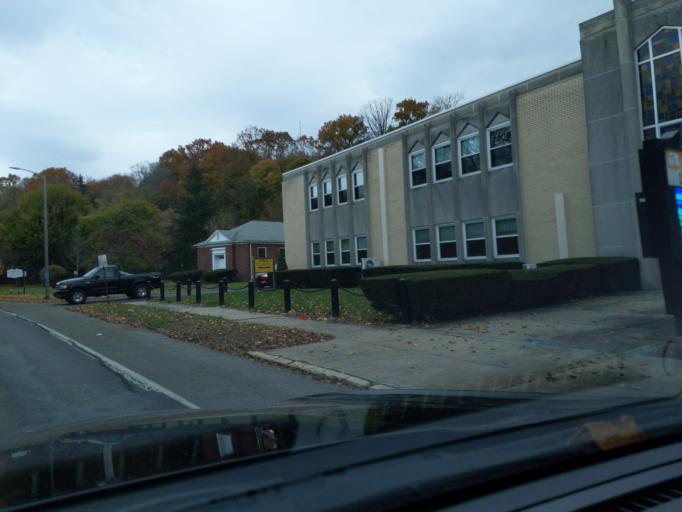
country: US
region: Pennsylvania
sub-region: Blair County
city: Lakemont
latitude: 40.4930
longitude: -78.4063
